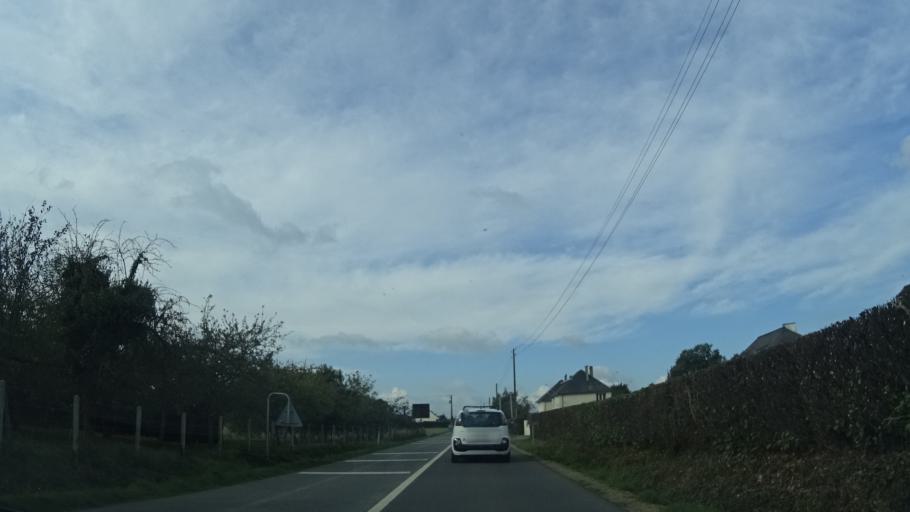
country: FR
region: Brittany
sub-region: Departement d'Ille-et-Vilaine
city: Combourg
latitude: 48.4142
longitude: -1.7620
